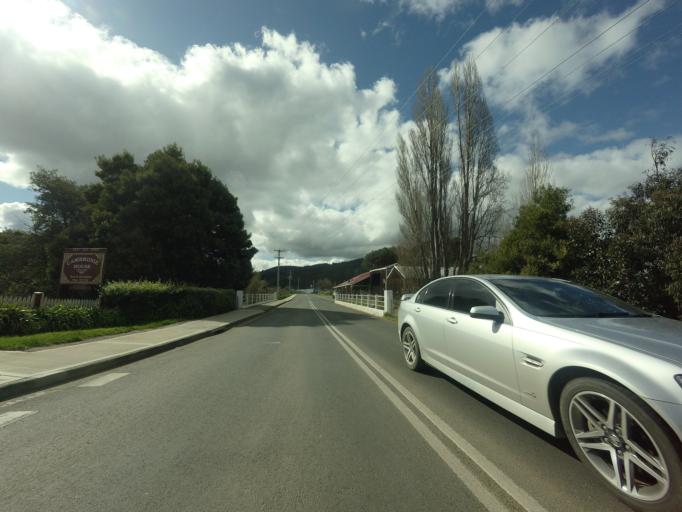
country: AU
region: Tasmania
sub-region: Huon Valley
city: Geeveston
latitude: -43.1668
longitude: 146.9261
